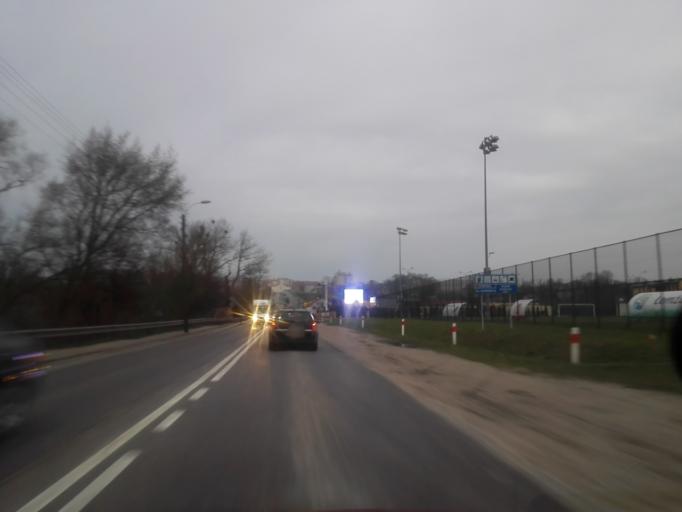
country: PL
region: Podlasie
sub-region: Powiat lomzynski
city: Piatnica
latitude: 53.1856
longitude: 22.0852
